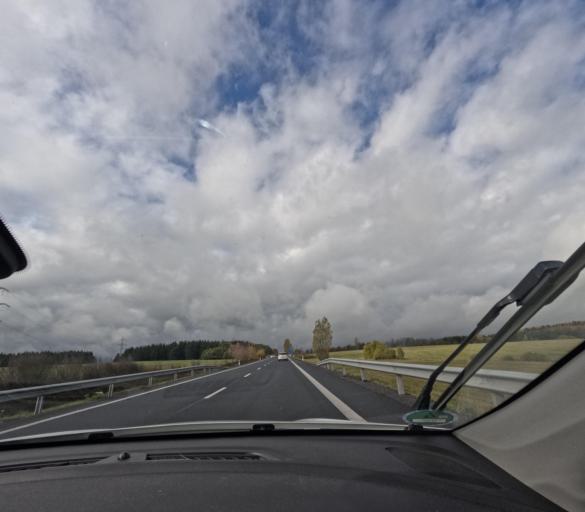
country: CZ
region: Karlovarsky
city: Bochov
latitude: 50.1471
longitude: 13.0674
